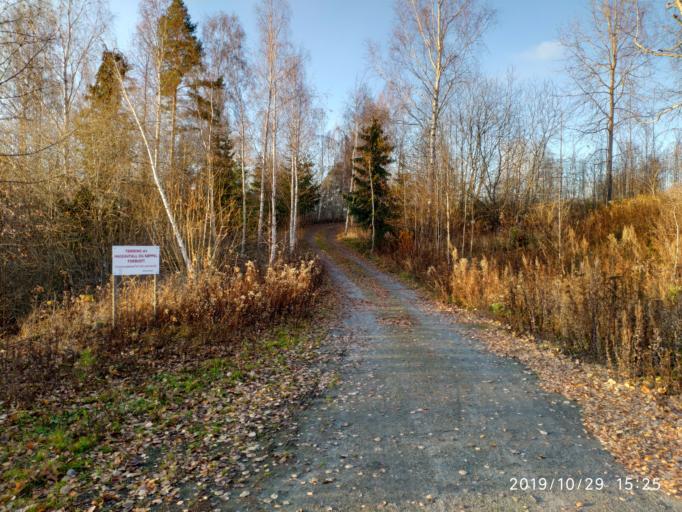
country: NO
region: Akershus
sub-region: Nes
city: Arnes
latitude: 60.1701
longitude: 11.5304
